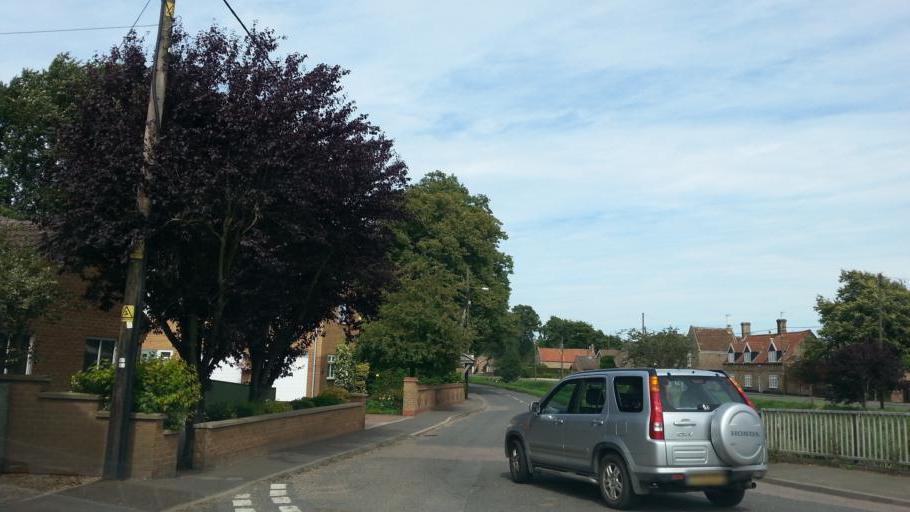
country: GB
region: England
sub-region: Norfolk
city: Outwell
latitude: 52.5978
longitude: 0.2106
